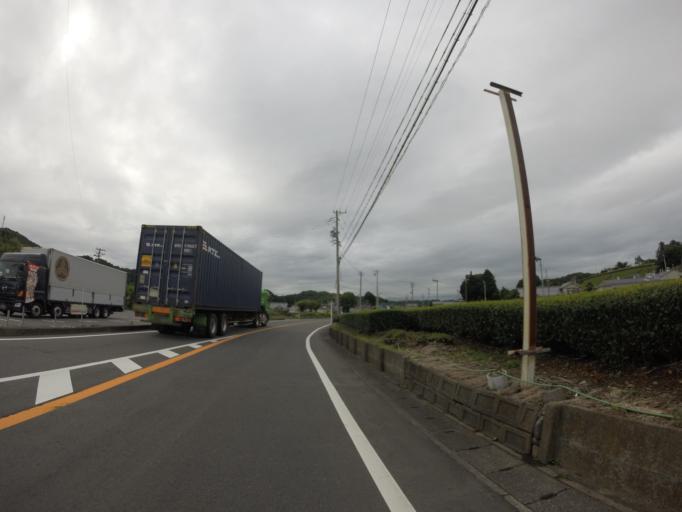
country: JP
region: Shizuoka
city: Sagara
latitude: 34.7269
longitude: 138.1633
